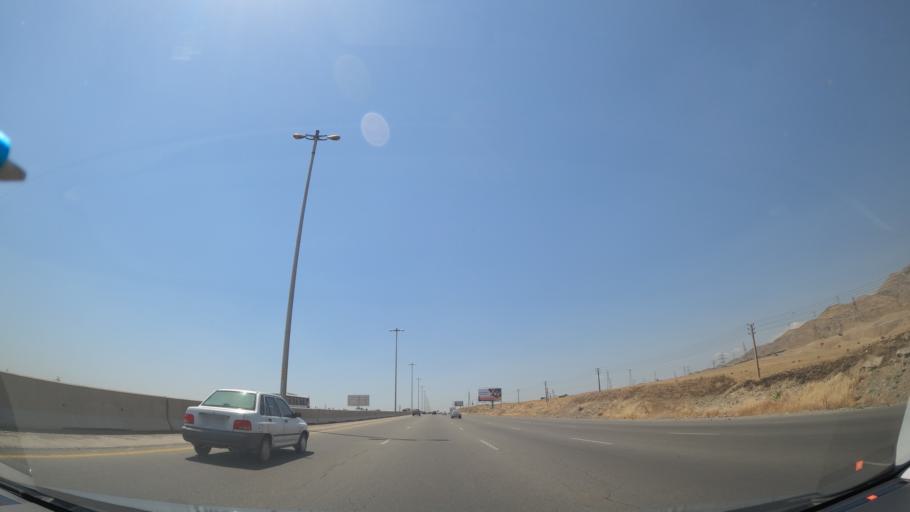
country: IR
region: Tehran
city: Shahr-e Qods
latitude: 35.7663
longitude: 51.0543
